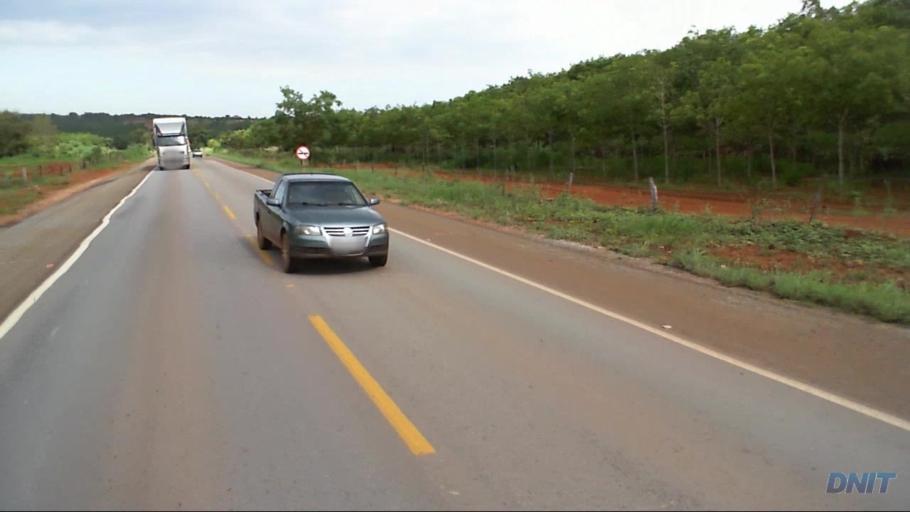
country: BR
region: Goias
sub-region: Barro Alto
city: Barro Alto
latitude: -14.8759
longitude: -48.9972
